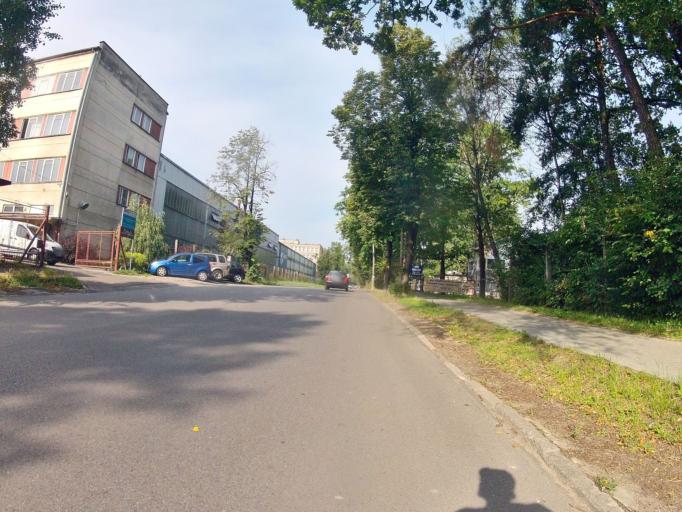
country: PL
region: Subcarpathian Voivodeship
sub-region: Powiat jasielski
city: Trzcinica
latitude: 49.7679
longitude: 21.4186
